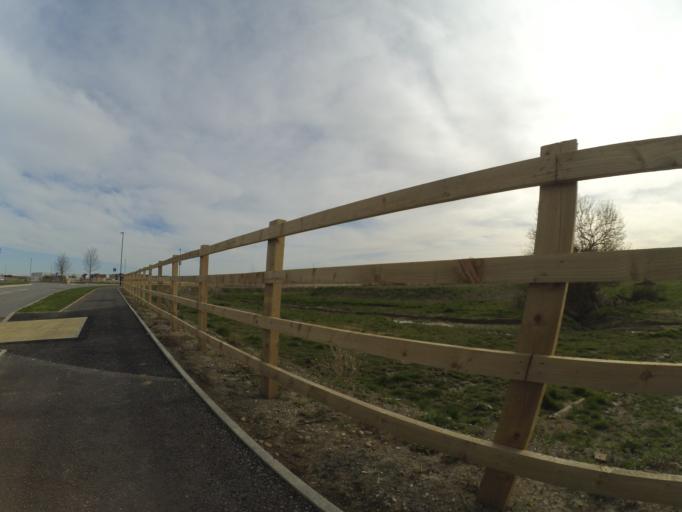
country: GB
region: England
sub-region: Warwickshire
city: Rugby
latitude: 52.3639
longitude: -1.1920
